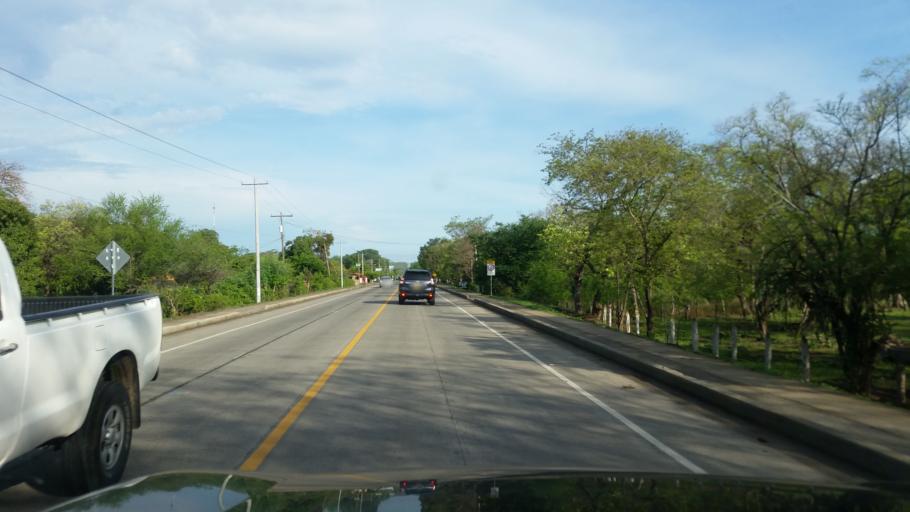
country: NI
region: Managua
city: Carlos Fonseca Amador
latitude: 12.1063
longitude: -86.5870
